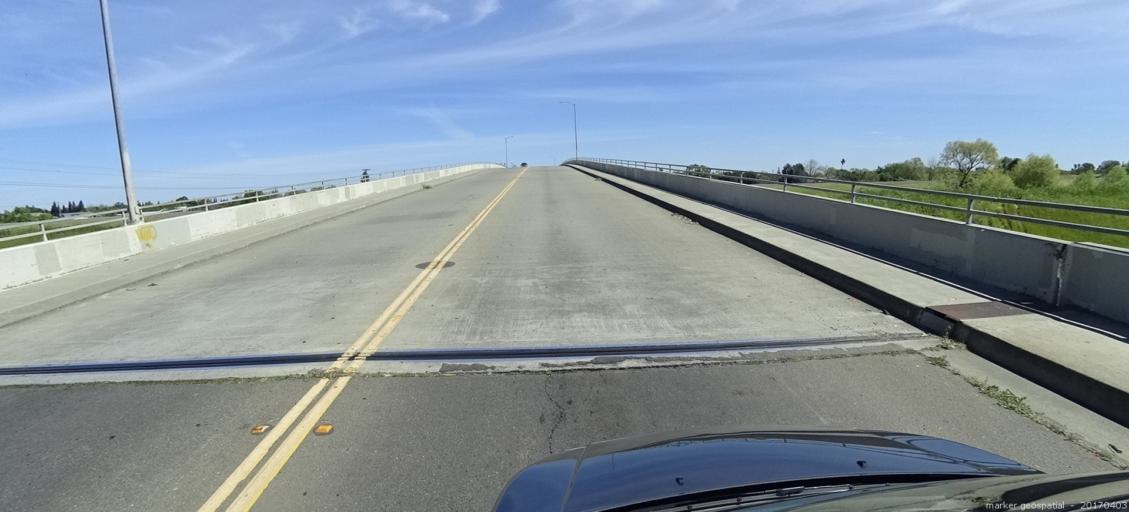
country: US
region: California
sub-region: Sacramento County
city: Sacramento
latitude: 38.6296
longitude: -121.4717
